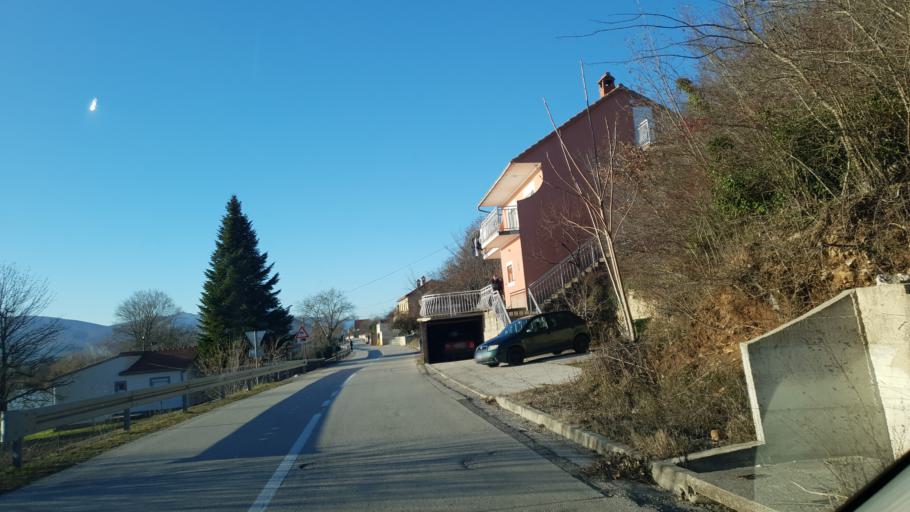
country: HR
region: Splitsko-Dalmatinska
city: Gala
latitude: 43.7312
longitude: 16.6935
